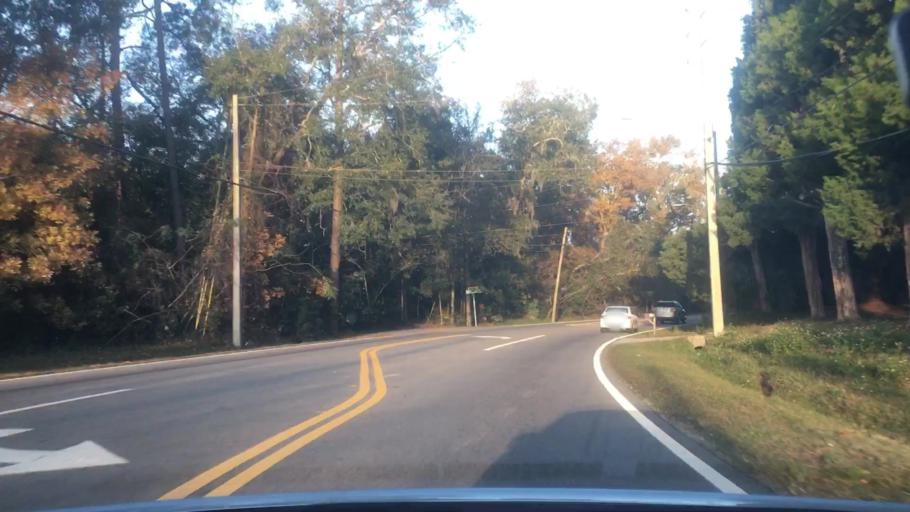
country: US
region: Florida
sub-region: Duval County
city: Jacksonville
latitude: 30.4611
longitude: -81.5797
